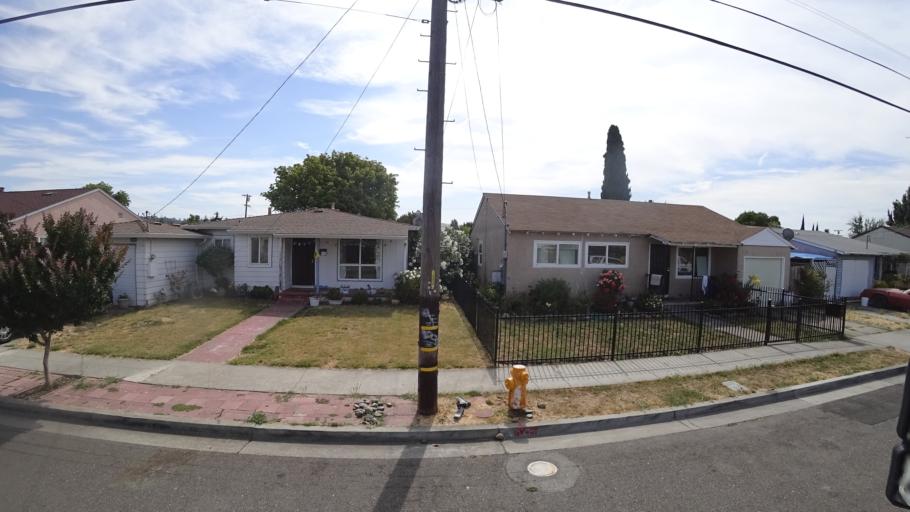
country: US
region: California
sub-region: Alameda County
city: Hayward
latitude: 37.6434
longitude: -122.0852
